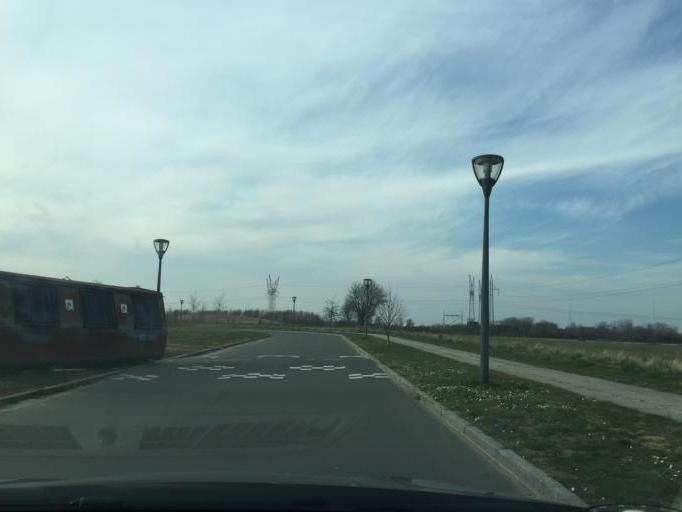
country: DK
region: South Denmark
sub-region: Odense Kommune
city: Neder Holluf
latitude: 55.3606
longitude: 10.5072
